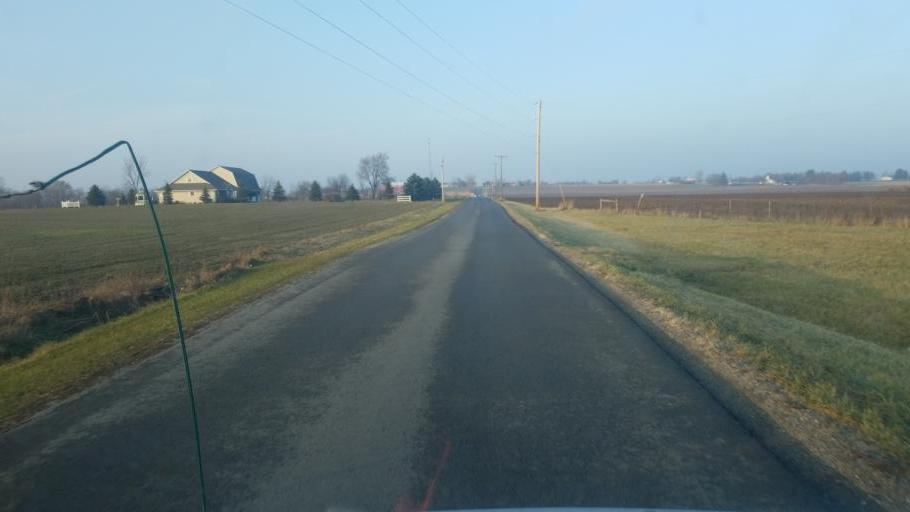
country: US
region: Ohio
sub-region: Wyandot County
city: Carey
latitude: 40.9537
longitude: -83.4292
